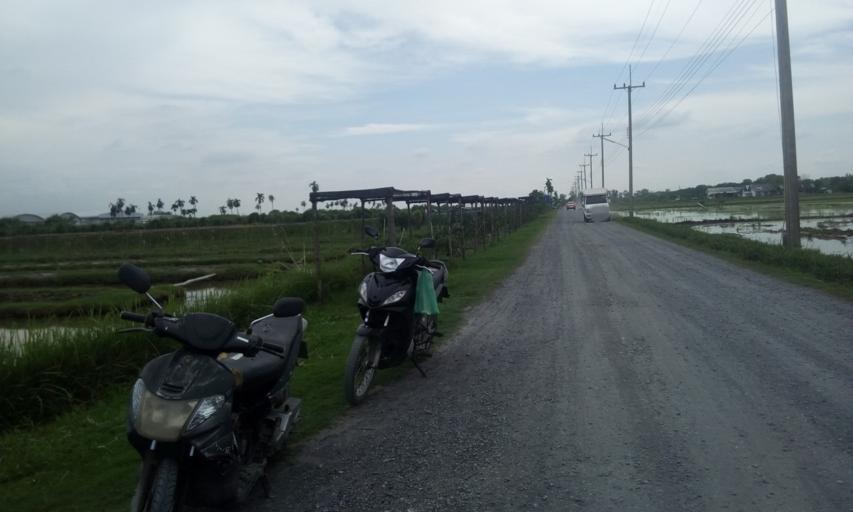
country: TH
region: Pathum Thani
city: Ban Lam Luk Ka
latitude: 13.9896
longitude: 100.8408
